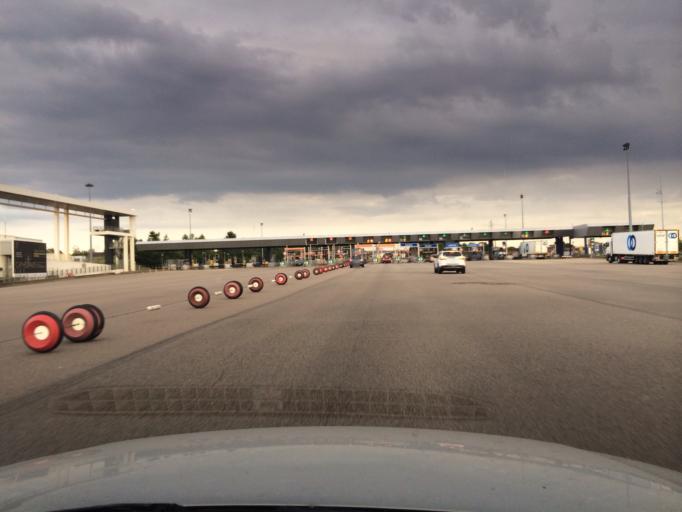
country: FR
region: Haute-Normandie
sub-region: Departement de l'Eure
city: Ande
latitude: 49.1927
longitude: 1.2316
